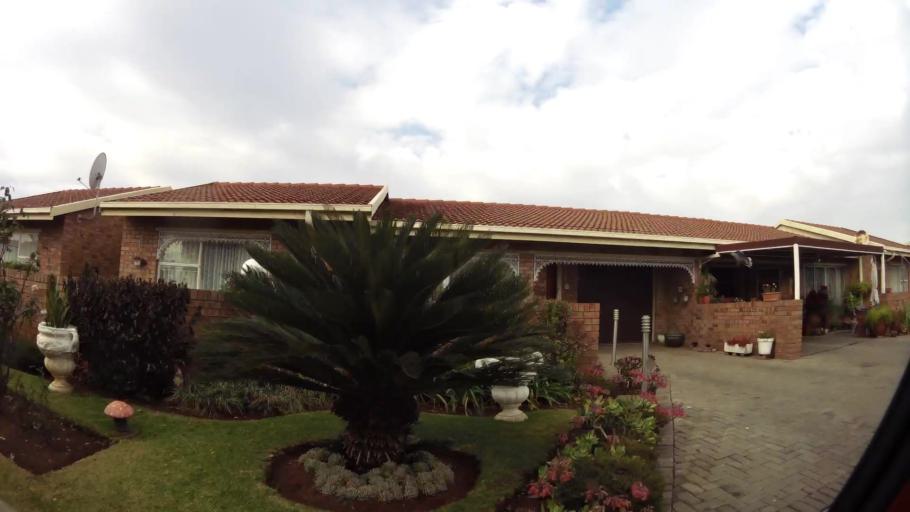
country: ZA
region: Gauteng
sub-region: Sedibeng District Municipality
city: Vanderbijlpark
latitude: -26.7061
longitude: 27.8270
